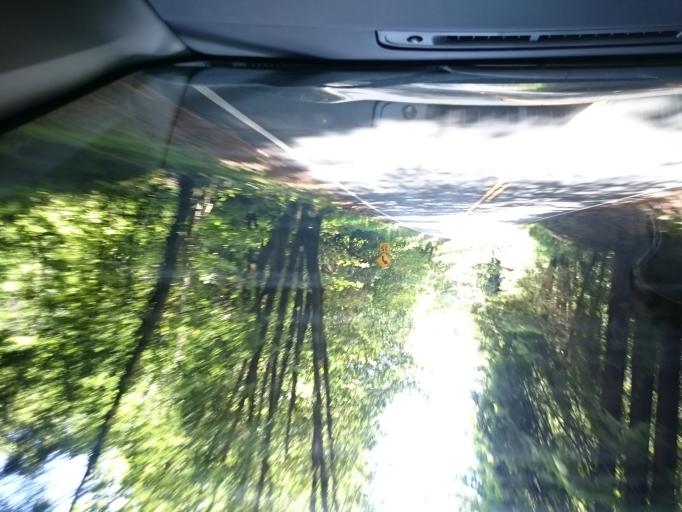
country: US
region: California
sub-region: Mendocino County
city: Fort Bragg
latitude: 39.1718
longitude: -123.6673
